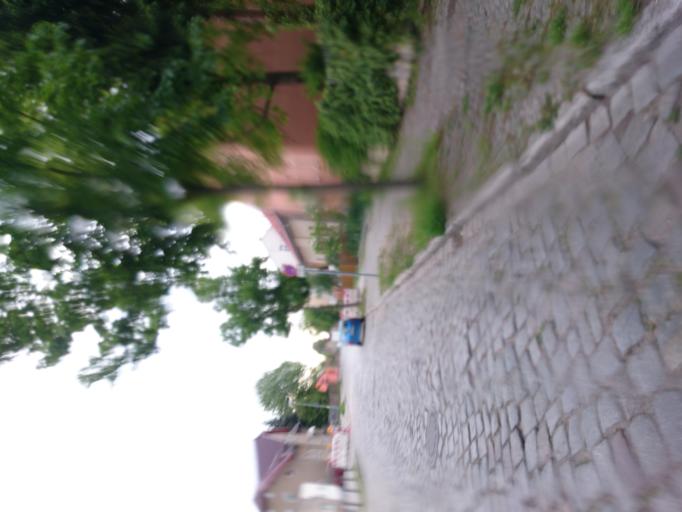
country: DE
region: Berlin
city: Blankenfelde
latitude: 52.6180
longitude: 13.3881
